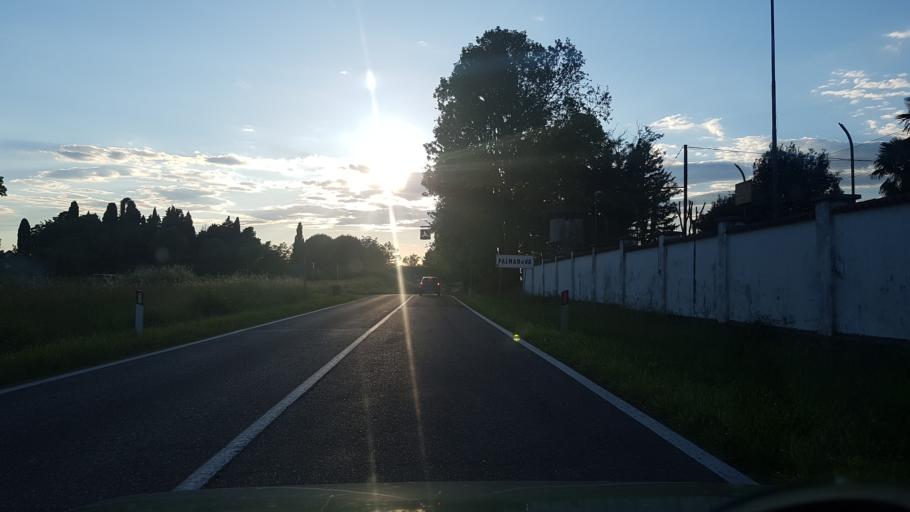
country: IT
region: Friuli Venezia Giulia
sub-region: Provincia di Udine
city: Sottoselva
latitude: 45.9074
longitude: 13.3191
